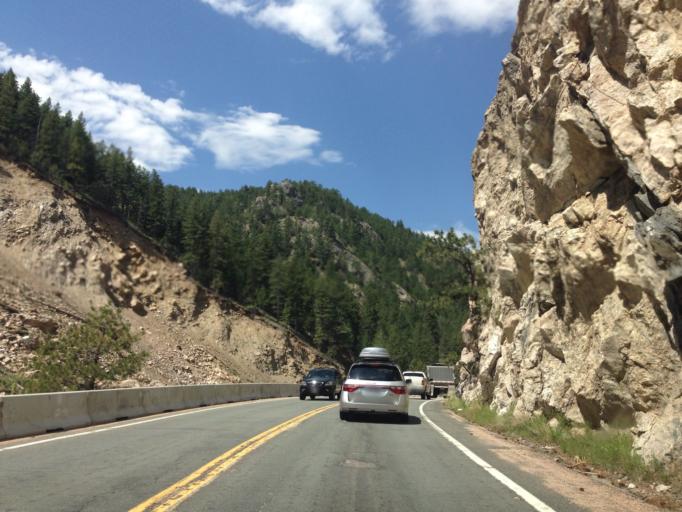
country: US
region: Colorado
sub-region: Larimer County
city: Estes Park
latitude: 40.4096
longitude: -105.3819
